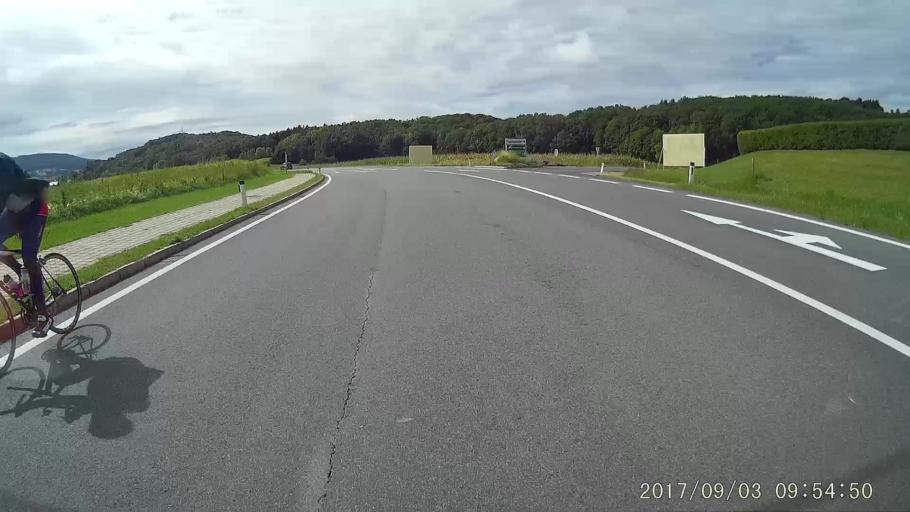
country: AT
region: Styria
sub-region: Politischer Bezirk Suedoststeiermark
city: Bad Gleichenberg
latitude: 46.8827
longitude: 15.8949
